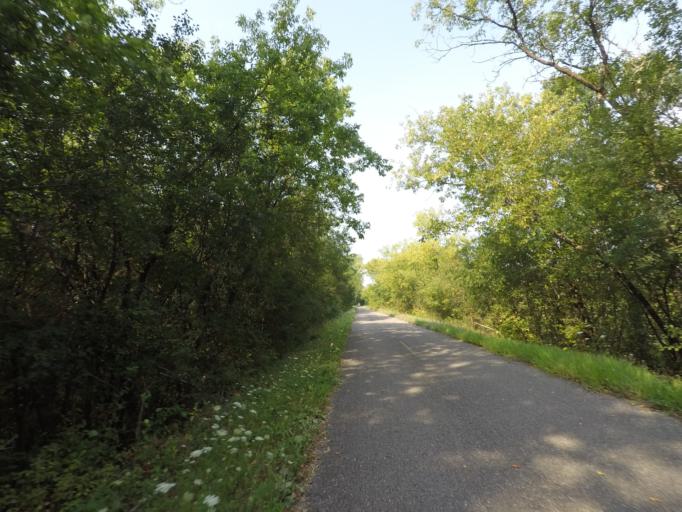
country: US
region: Wisconsin
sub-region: Waukesha County
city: Dousman
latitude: 43.0166
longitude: -88.4297
